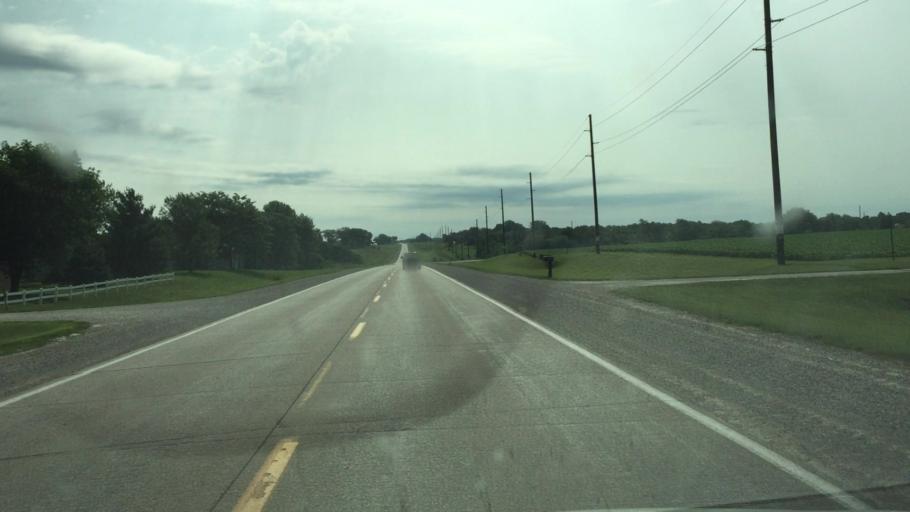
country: US
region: Illinois
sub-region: Hancock County
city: Nauvoo
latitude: 40.6390
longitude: -91.5497
